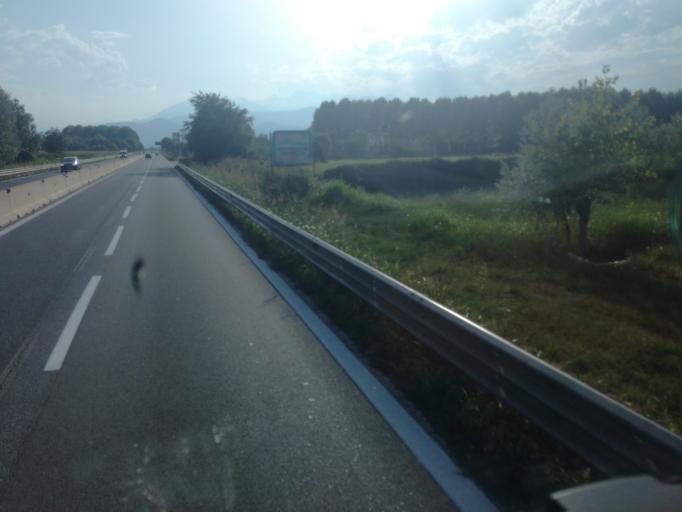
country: IT
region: Piedmont
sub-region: Provincia di Torino
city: Riva
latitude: 44.8903
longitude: 7.3889
